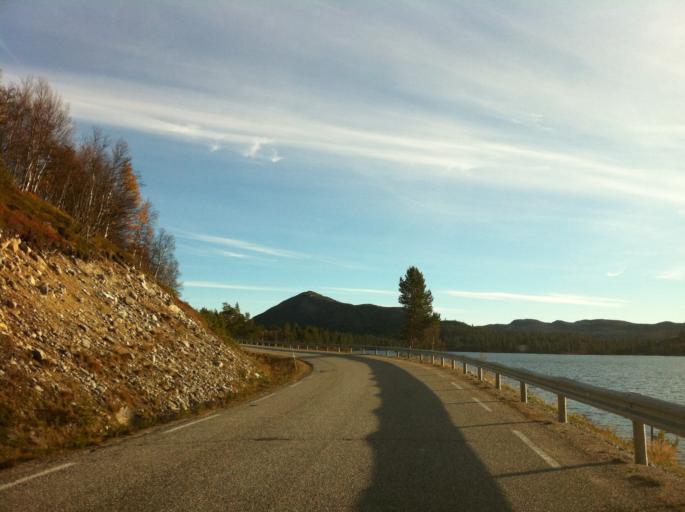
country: NO
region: Hedmark
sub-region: Engerdal
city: Engerdal
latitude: 62.1082
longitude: 12.0205
